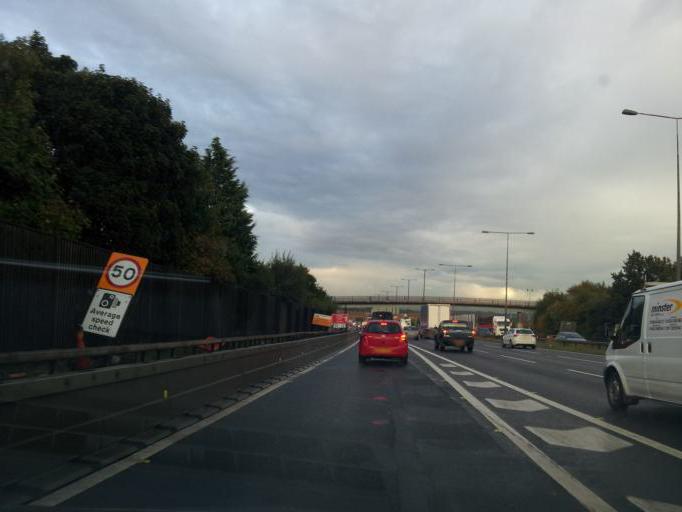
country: GB
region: England
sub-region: Borough of Bury
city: Prestwich
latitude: 53.5532
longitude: -2.2538
